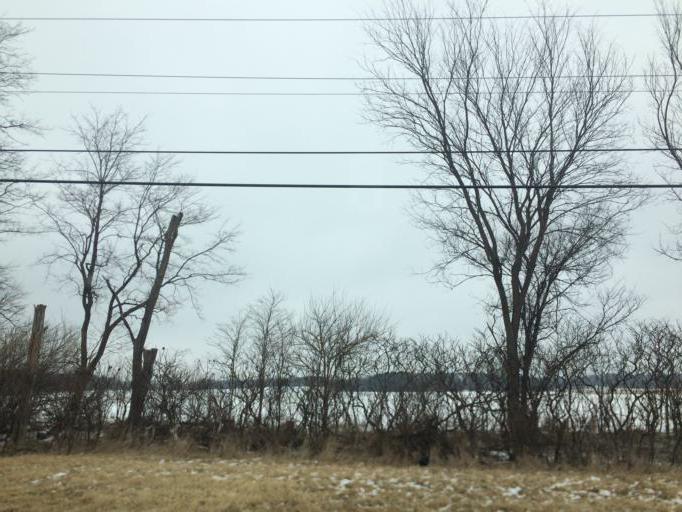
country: US
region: Illinois
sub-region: McHenry County
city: Harvard
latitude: 42.3527
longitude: -88.5499
